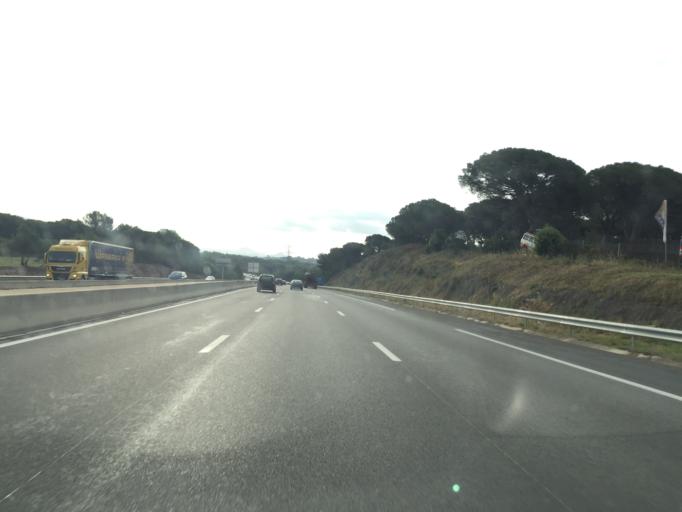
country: FR
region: Provence-Alpes-Cote d'Azur
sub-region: Departement du Var
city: Puget-sur-Argens
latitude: 43.4572
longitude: 6.6987
